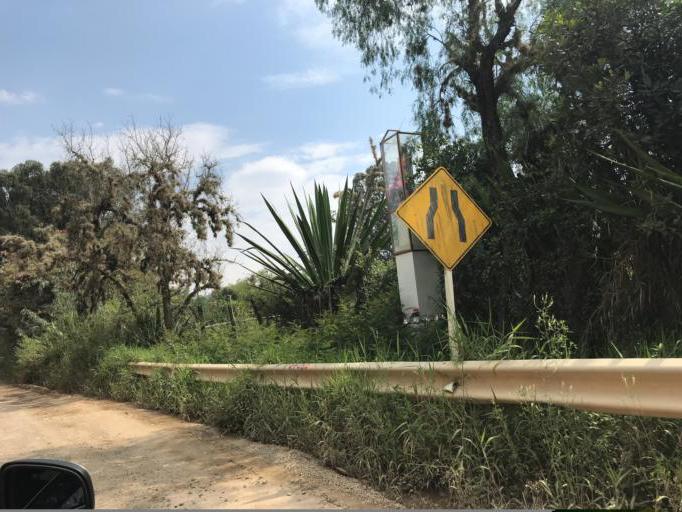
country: CO
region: Boyaca
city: Villa de Leiva
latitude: 5.6520
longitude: -73.5761
